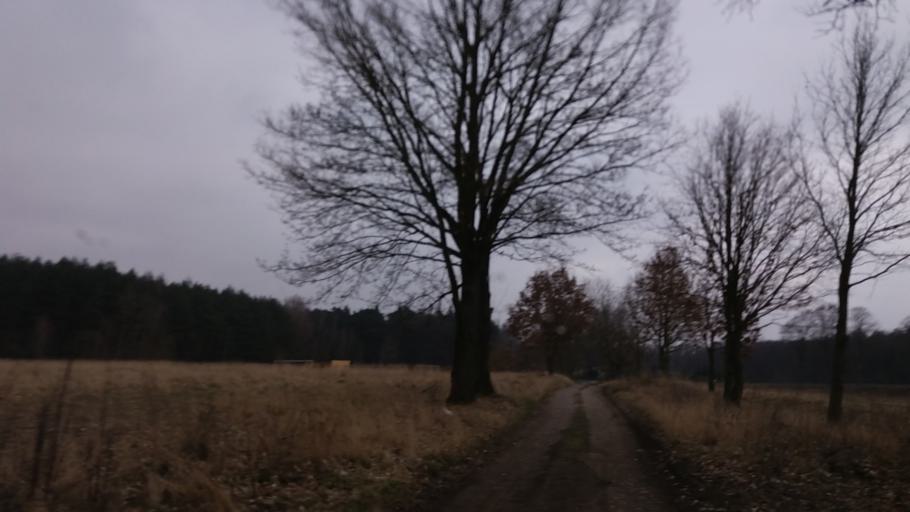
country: PL
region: West Pomeranian Voivodeship
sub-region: Powiat choszczenski
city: Recz
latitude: 53.1819
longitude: 15.5173
